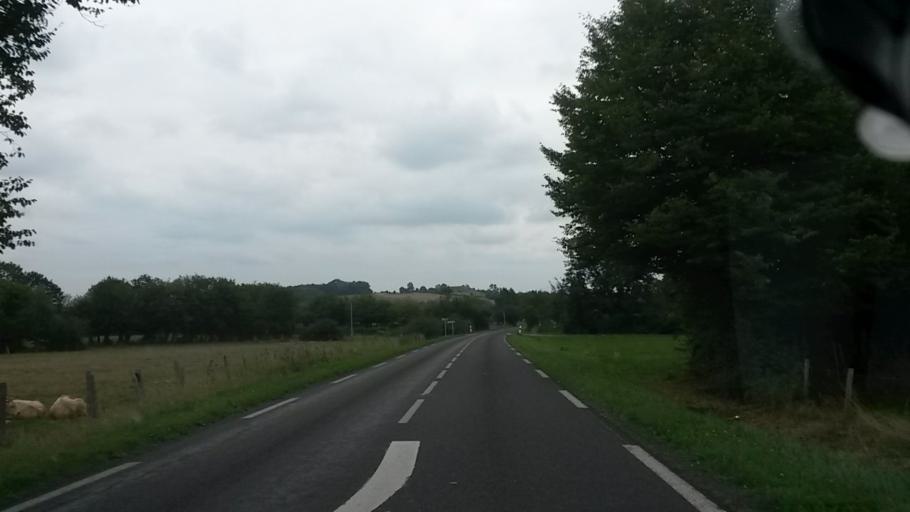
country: FR
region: Haute-Normandie
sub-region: Departement de la Seine-Maritime
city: Forges-les-Eaux
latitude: 49.5795
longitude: 1.5441
